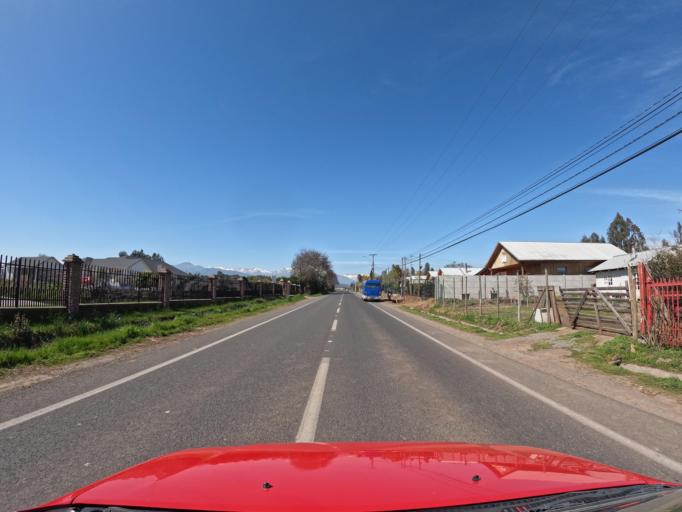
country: CL
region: Maule
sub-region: Provincia de Curico
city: Teno
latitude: -34.9653
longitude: -71.0424
